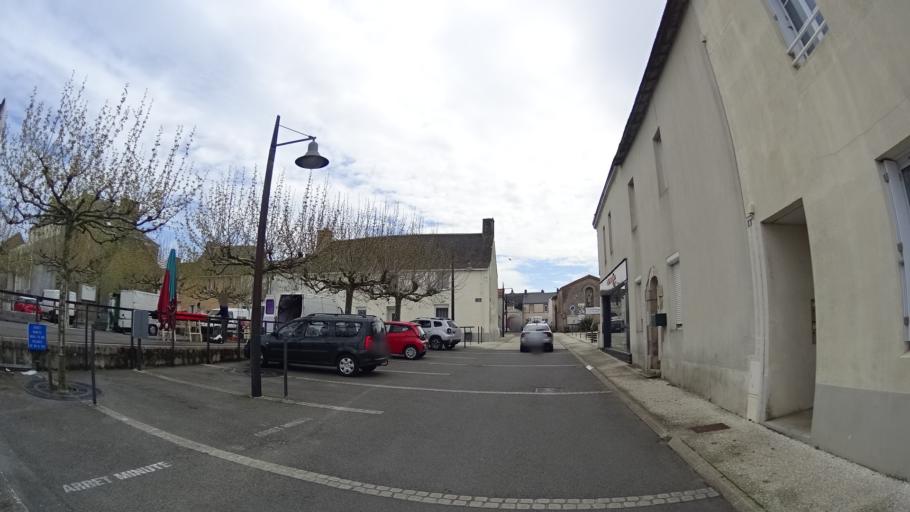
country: FR
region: Pays de la Loire
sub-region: Departement de la Loire-Atlantique
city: Bourgneuf-en-Retz
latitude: 47.0428
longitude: -1.9535
